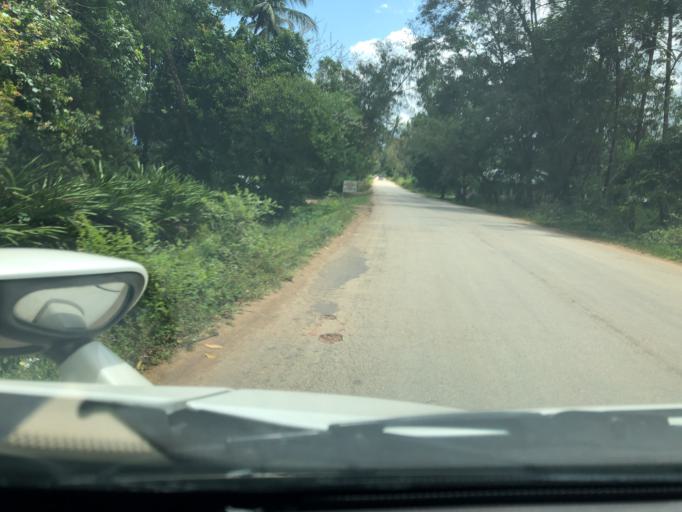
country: TZ
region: Zanzibar Central/South
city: Koani
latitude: -6.0669
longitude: 39.2512
